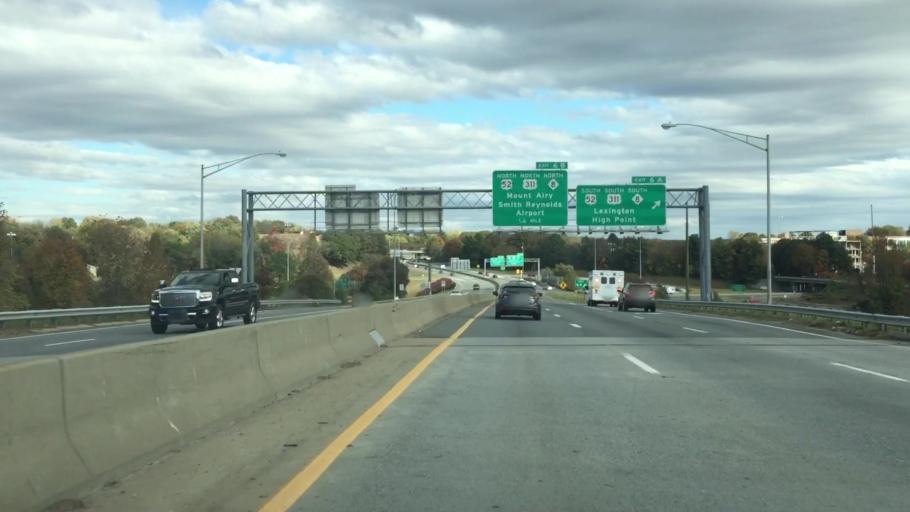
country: US
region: North Carolina
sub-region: Forsyth County
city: Winston-Salem
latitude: 36.0936
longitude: -80.2363
